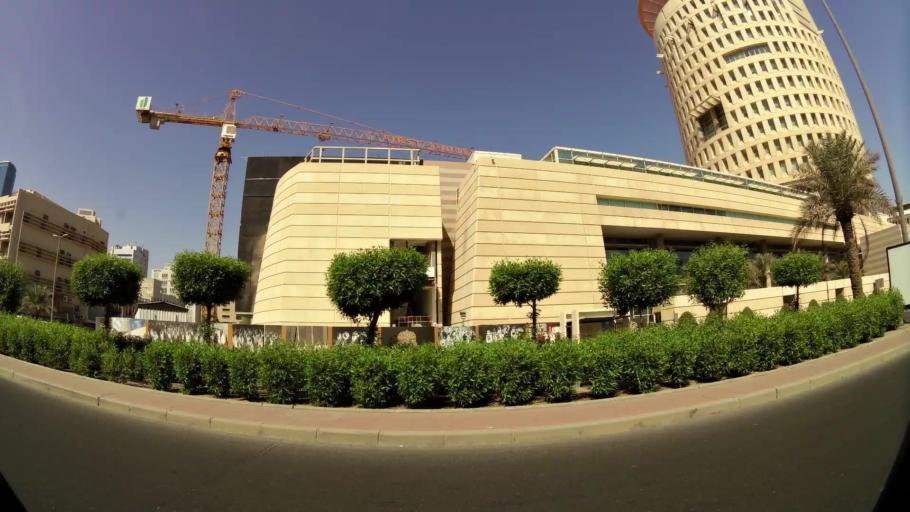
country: KW
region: Al Asimah
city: Kuwait City
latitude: 29.3711
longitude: 47.9814
